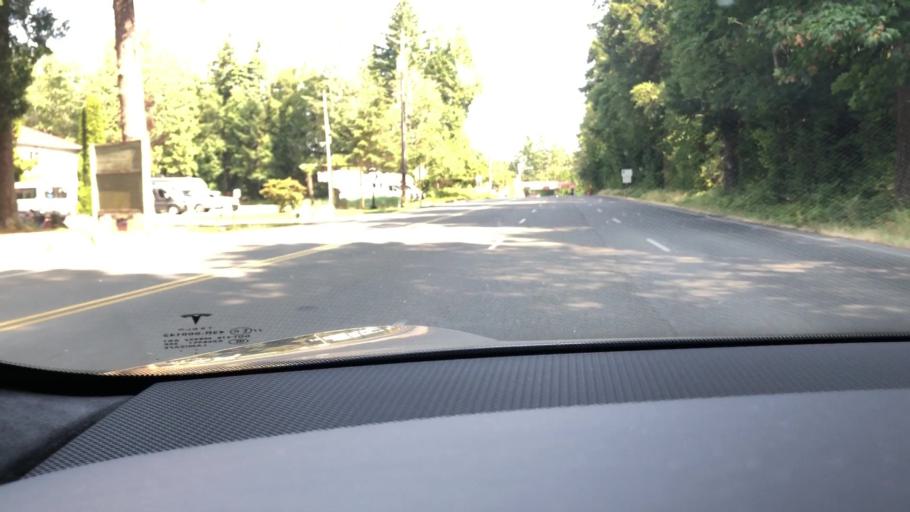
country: US
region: Washington
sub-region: Whatcom County
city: Point Roberts
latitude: 48.9994
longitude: -123.0680
